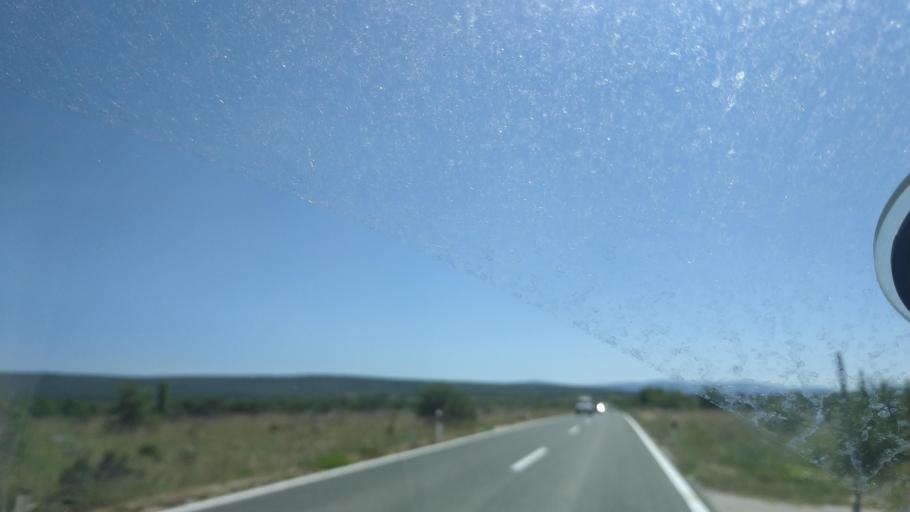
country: HR
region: Sibensko-Kniniska
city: Drnis
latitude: 43.8316
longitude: 16.0901
